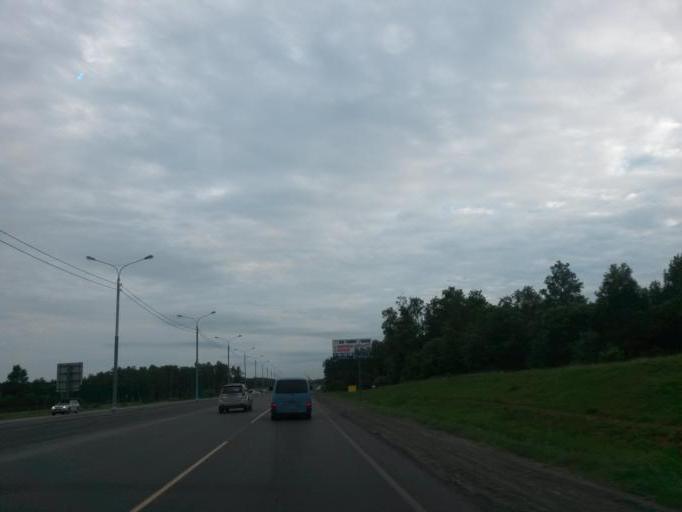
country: RU
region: Moskovskaya
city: L'vovskiy
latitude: 55.3195
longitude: 37.5575
